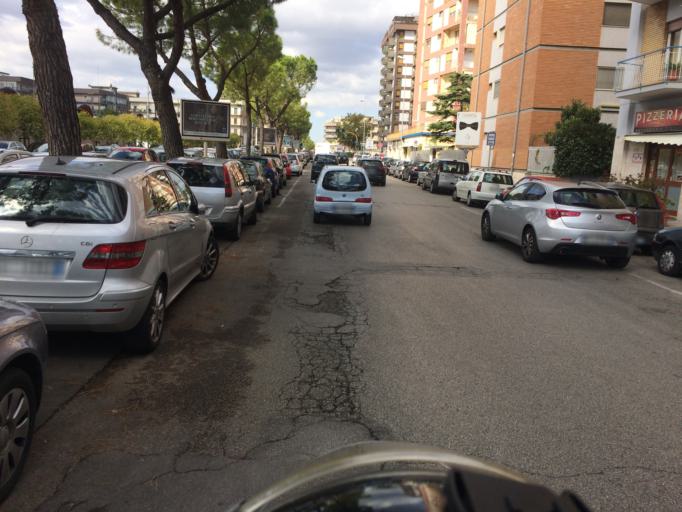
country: IT
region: Apulia
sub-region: Provincia di Bari
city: Bari
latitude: 41.1073
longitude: 16.8671
